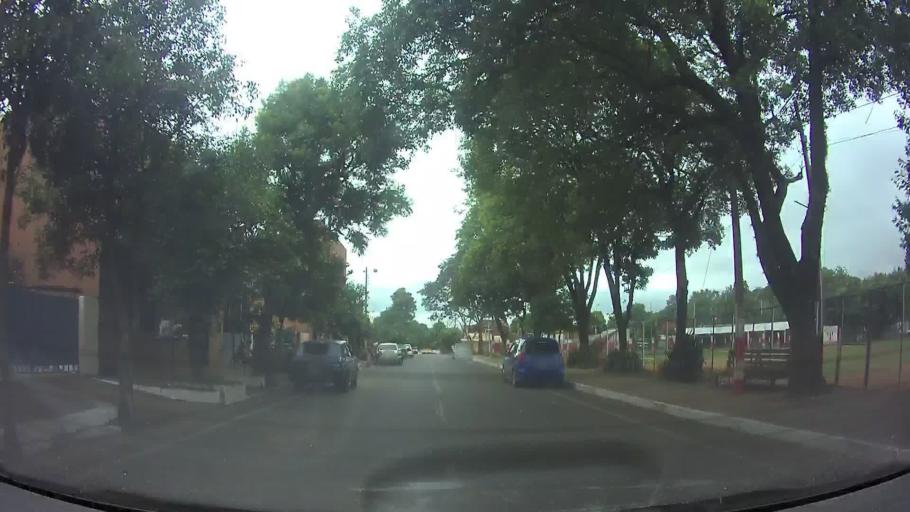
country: PY
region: Central
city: San Lorenzo
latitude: -25.2689
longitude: -57.5012
